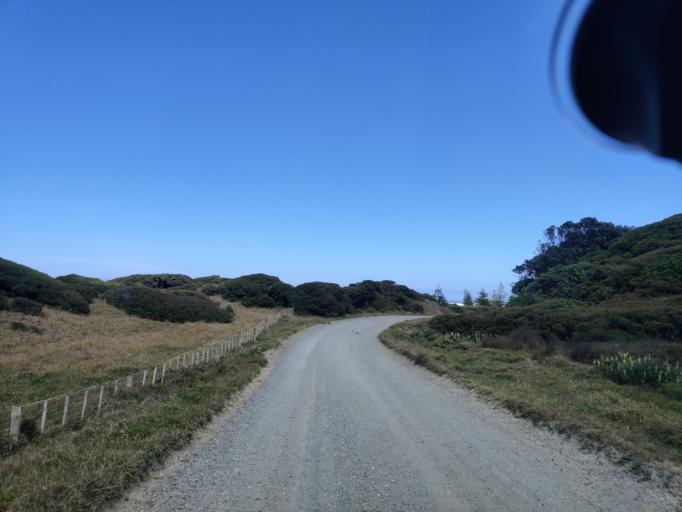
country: NZ
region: Northland
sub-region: Far North District
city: Kaitaia
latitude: -34.8985
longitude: 173.0907
